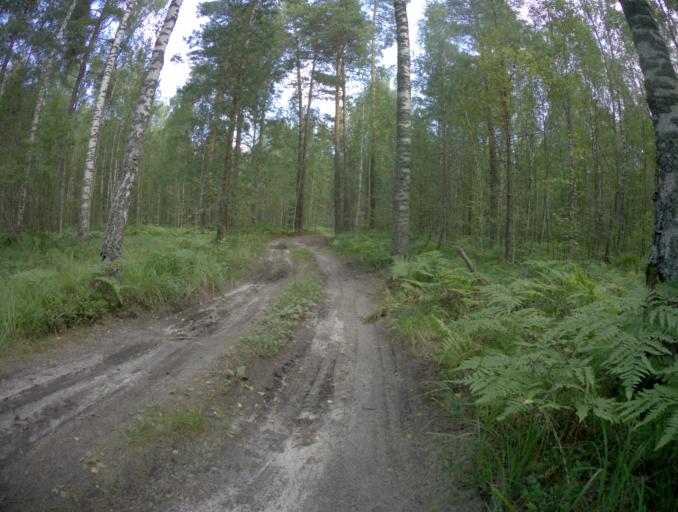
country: RU
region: Vladimir
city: Raduzhnyy
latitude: 55.9514
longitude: 40.1963
